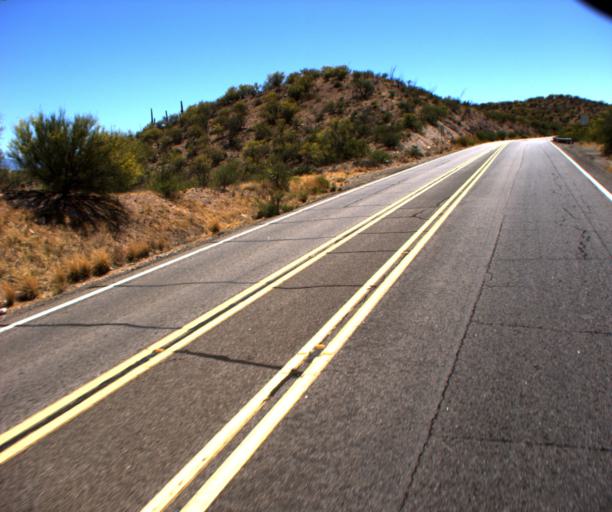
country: US
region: Arizona
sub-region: Pinal County
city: Mammoth
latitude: 32.6724
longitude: -110.6640
